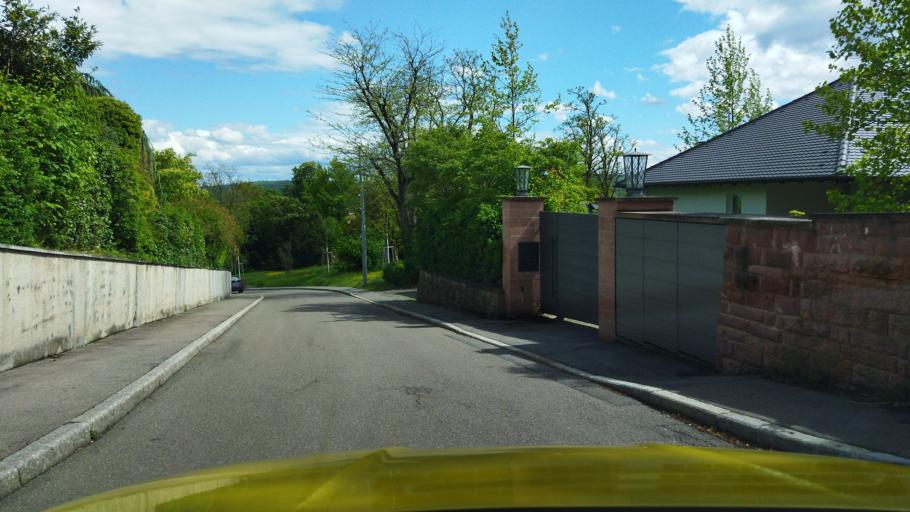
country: DE
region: Baden-Wuerttemberg
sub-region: Regierungsbezirk Stuttgart
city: Stuttgart
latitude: 48.7929
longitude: 9.1668
